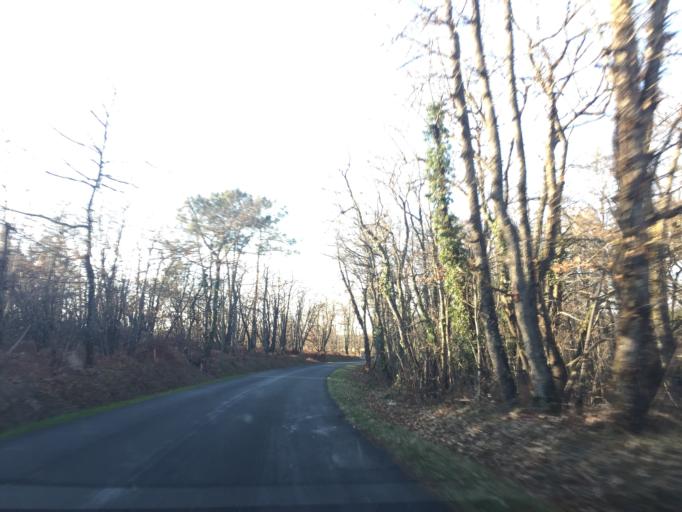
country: FR
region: Aquitaine
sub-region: Departement de la Dordogne
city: Riberac
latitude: 45.2106
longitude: 0.3020
